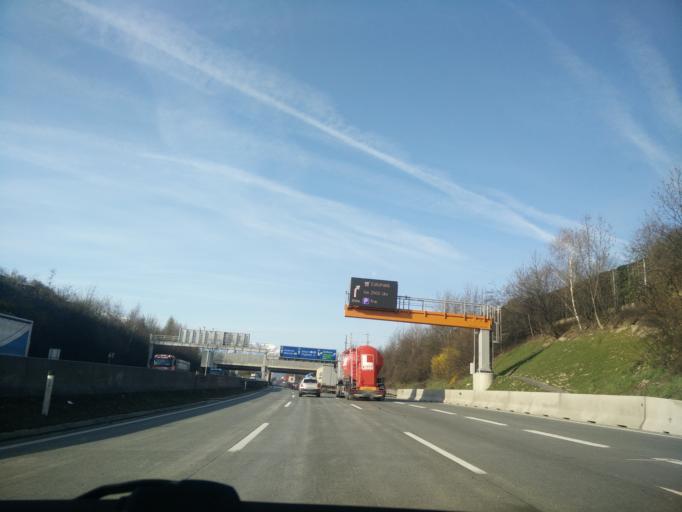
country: AT
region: Salzburg
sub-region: Politischer Bezirk Salzburg-Umgebung
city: Bergheim
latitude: 47.8235
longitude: 13.0105
